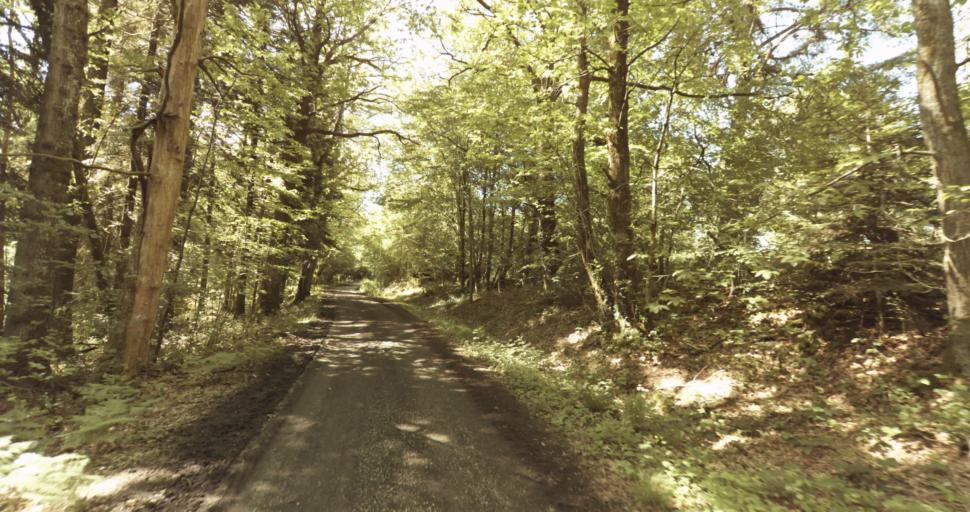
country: FR
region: Limousin
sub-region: Departement de la Haute-Vienne
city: Le Vigen
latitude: 45.7267
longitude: 1.3030
